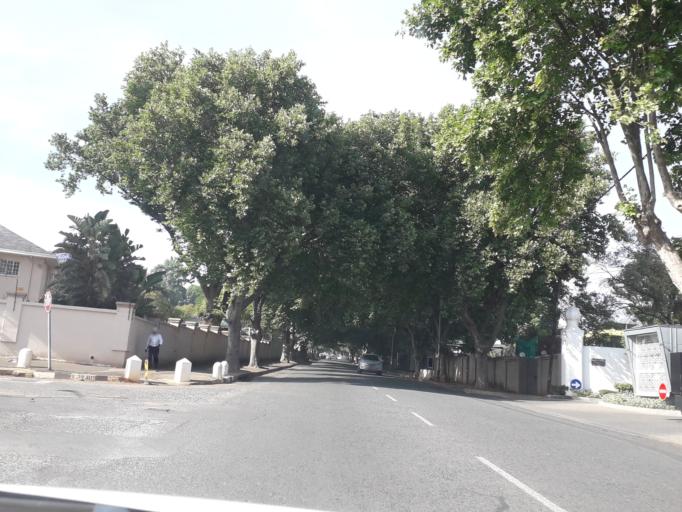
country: ZA
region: Gauteng
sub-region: City of Johannesburg Metropolitan Municipality
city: Johannesburg
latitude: -26.1634
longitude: 28.0578
